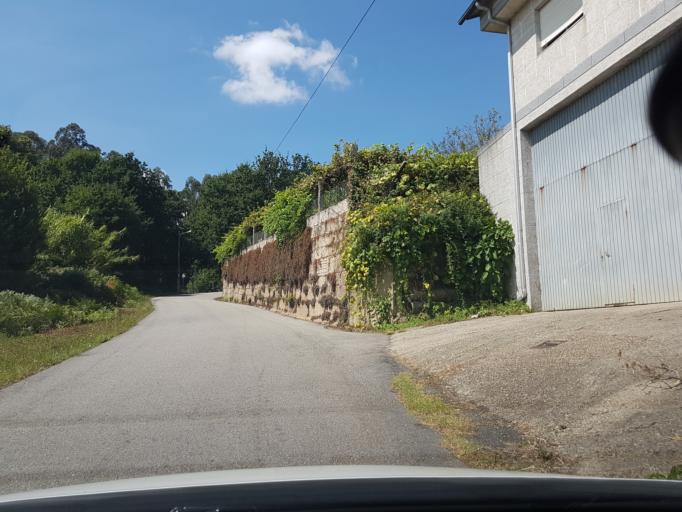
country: ES
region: Galicia
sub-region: Provincia de Pontevedra
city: Porrino
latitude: 42.2148
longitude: -8.6299
